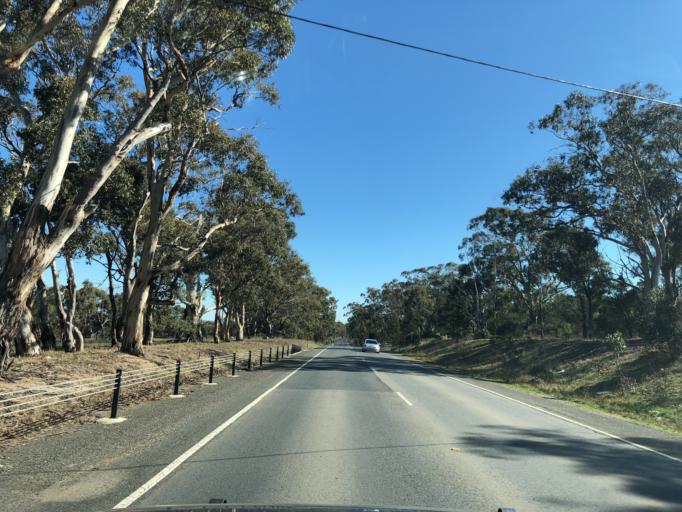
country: AU
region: Victoria
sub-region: Melton
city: Melton West
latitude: -37.6123
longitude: 144.5658
